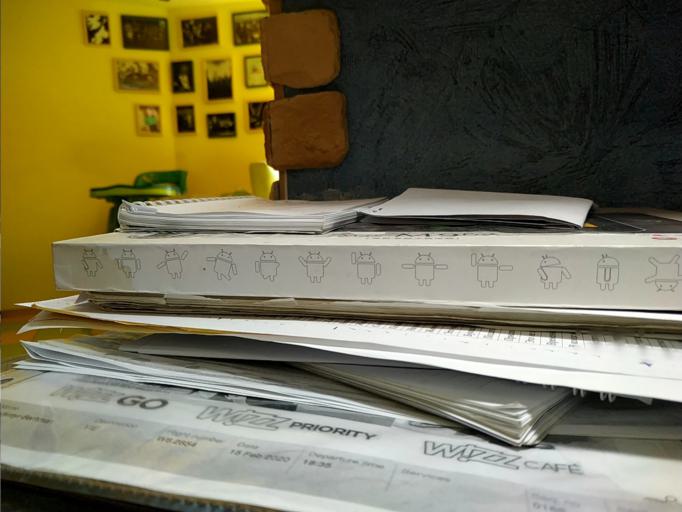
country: RU
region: Novgorod
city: Utorgosh
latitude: 58.2189
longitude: 29.9453
